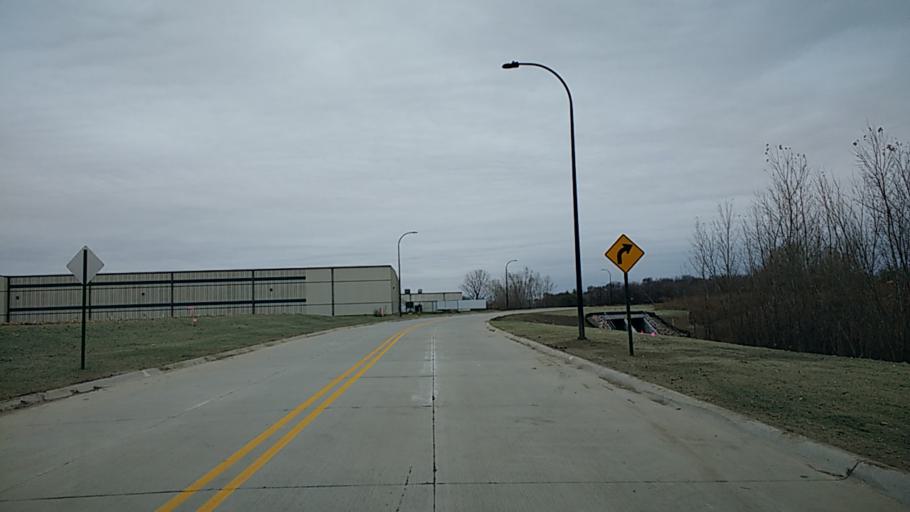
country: US
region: Iowa
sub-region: Woodbury County
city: Sergeant Bluff
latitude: 42.4175
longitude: -96.3745
